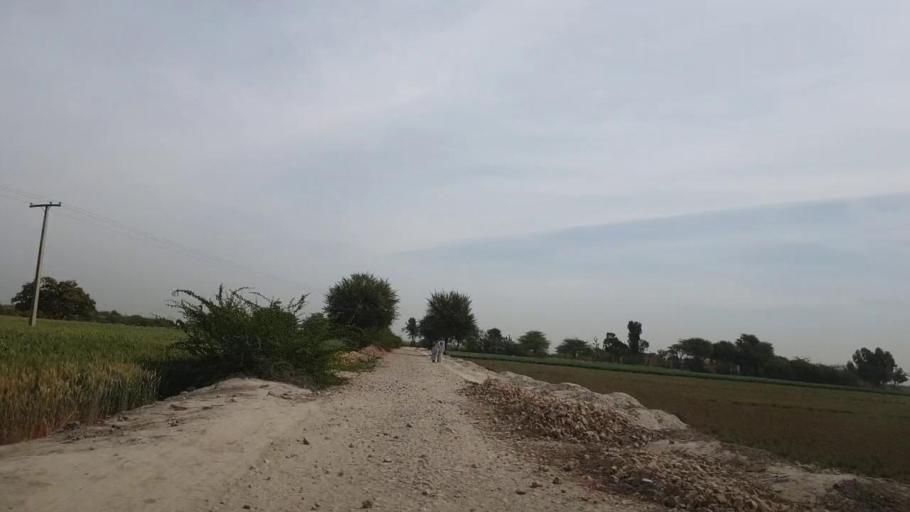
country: PK
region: Sindh
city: Kunri
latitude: 25.1830
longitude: 69.5895
